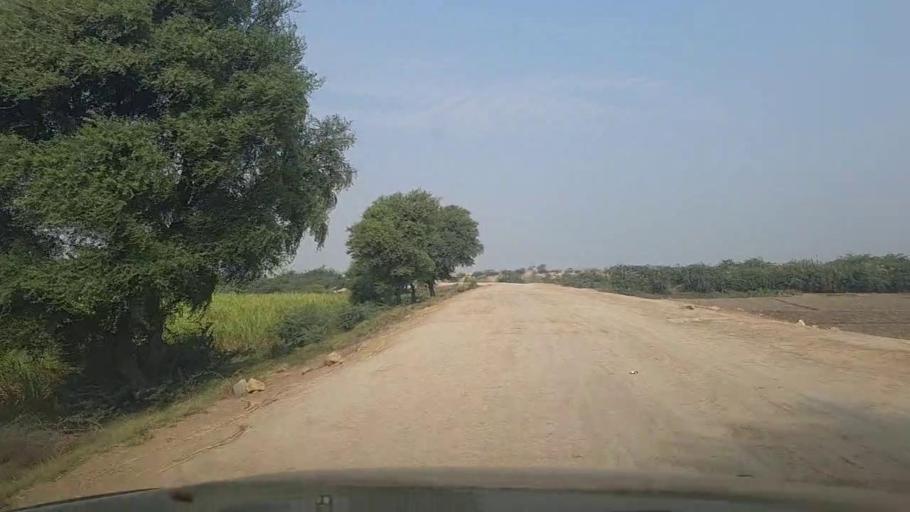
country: PK
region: Sindh
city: Bulri
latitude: 25.0315
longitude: 68.2798
